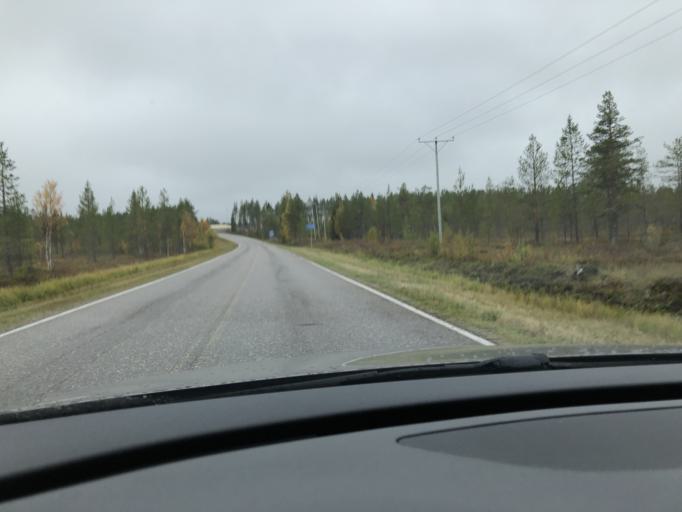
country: FI
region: Lapland
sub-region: Itae-Lappi
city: Posio
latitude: 66.1213
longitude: 28.1836
